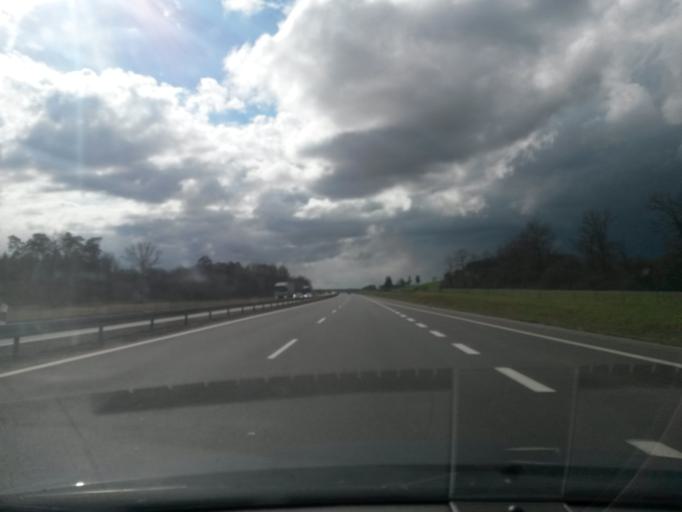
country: PL
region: Greater Poland Voivodeship
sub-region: Powiat wrzesinski
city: Nekla
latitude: 52.3171
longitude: 17.4122
